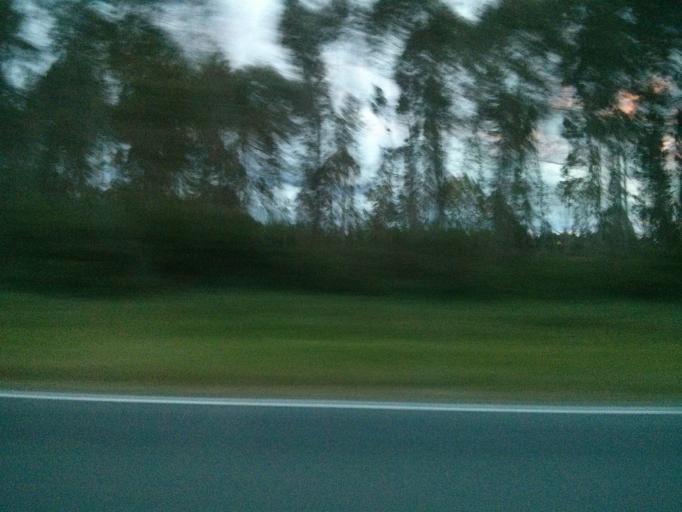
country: NZ
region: Canterbury
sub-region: Waimakariri District
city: Kaiapoi
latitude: -43.3871
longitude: 172.5644
